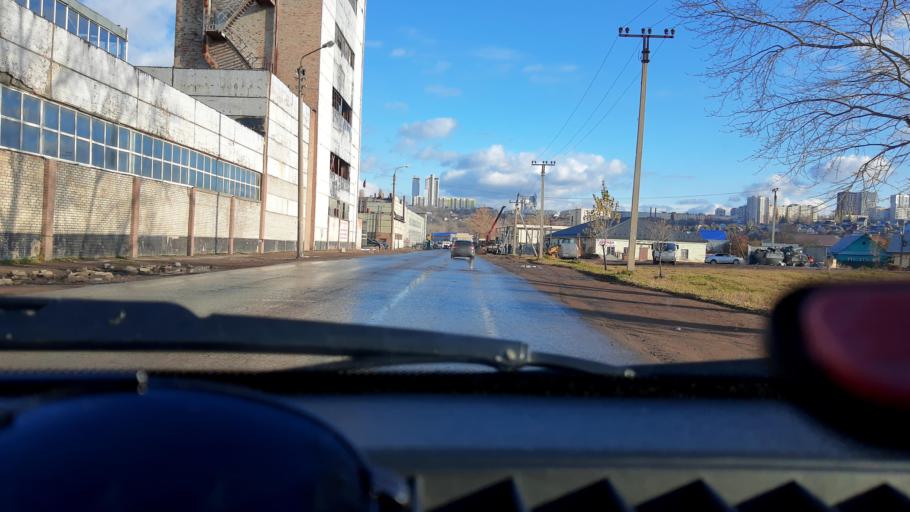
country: RU
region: Bashkortostan
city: Ufa
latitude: 54.7461
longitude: 55.9169
